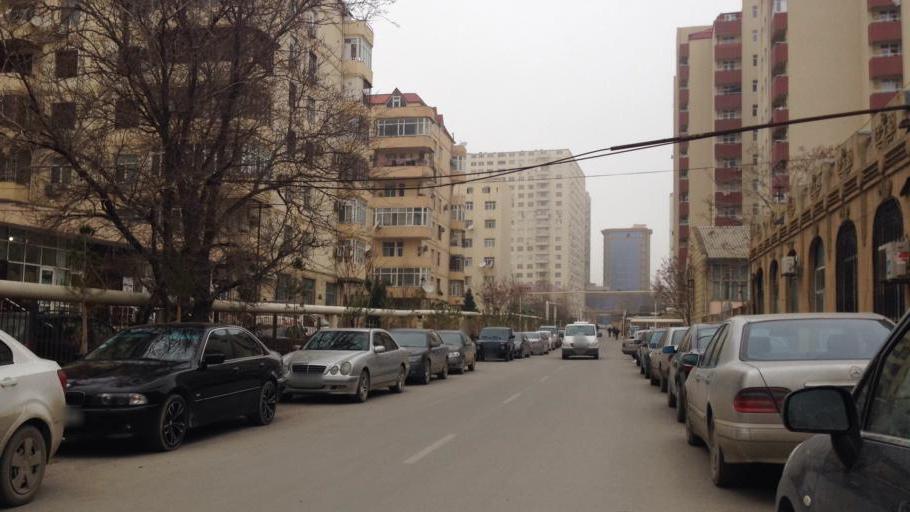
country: AZ
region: Baki
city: Baku
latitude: 40.3849
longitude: 49.8723
